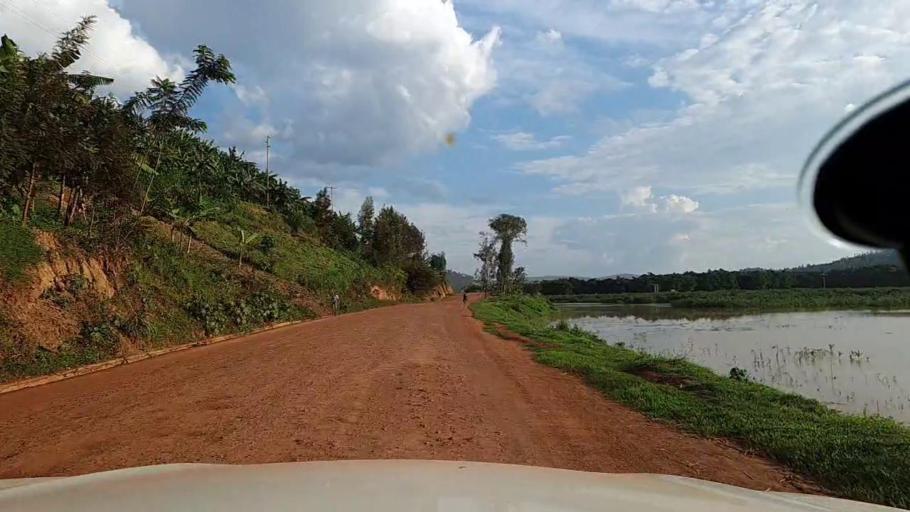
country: RW
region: Kigali
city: Kigali
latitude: -1.9356
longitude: 29.9977
